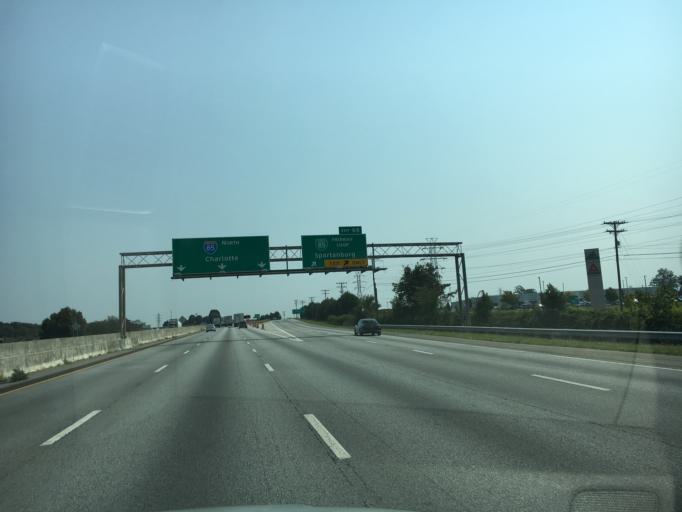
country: US
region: South Carolina
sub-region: Spartanburg County
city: Fairforest
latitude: 34.9634
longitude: -82.0391
